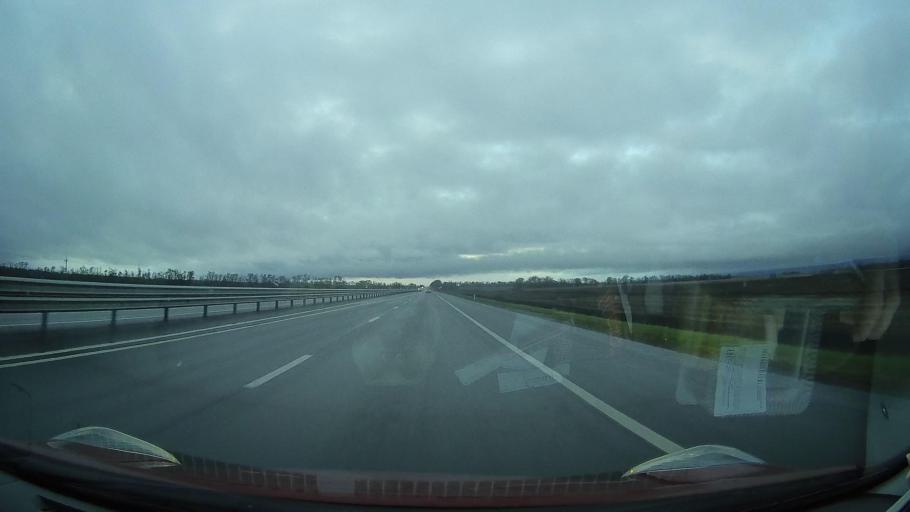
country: RU
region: Stavropol'skiy
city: Zavetnoye
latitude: 44.7840
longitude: 41.5241
